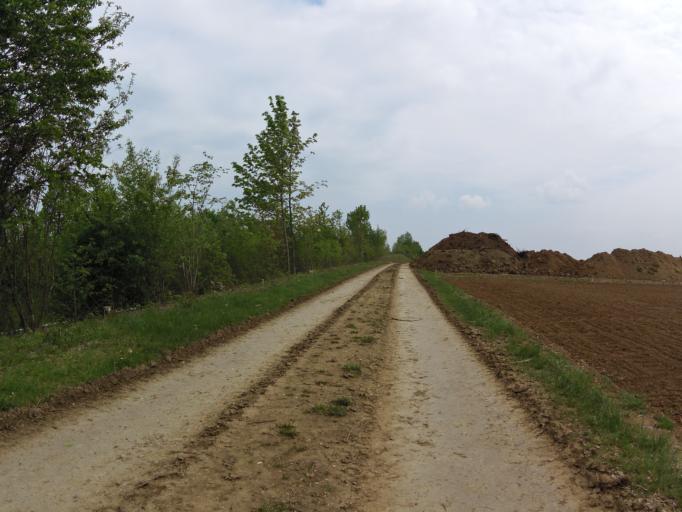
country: DE
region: Bavaria
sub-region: Regierungsbezirk Unterfranken
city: Kurnach
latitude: 49.8518
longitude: 10.0442
